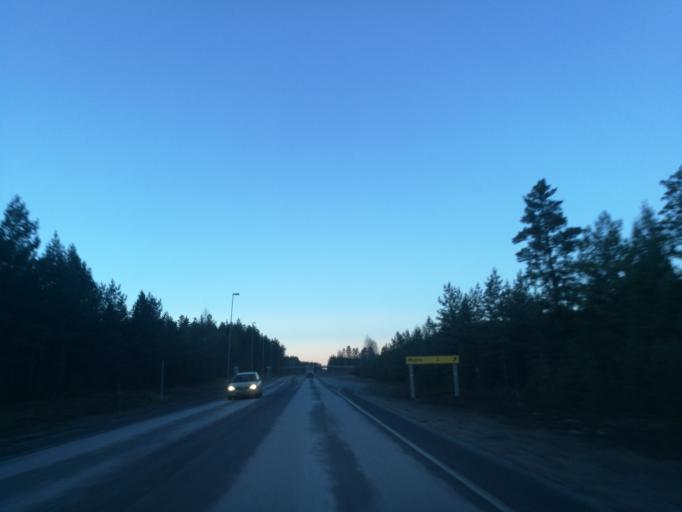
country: NO
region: Hedmark
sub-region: Eidskog
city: Skotterud
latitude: 59.9548
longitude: 12.1659
